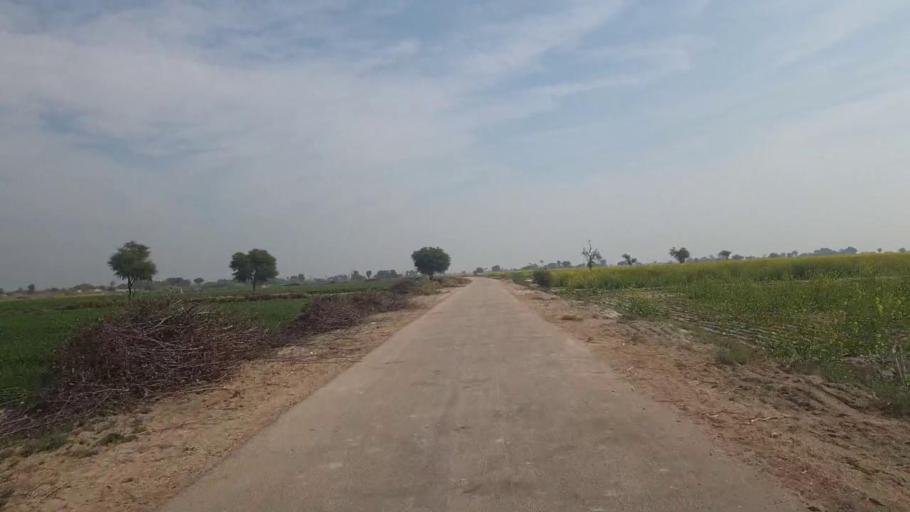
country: PK
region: Sindh
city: Nawabshah
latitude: 26.1240
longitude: 68.4919
